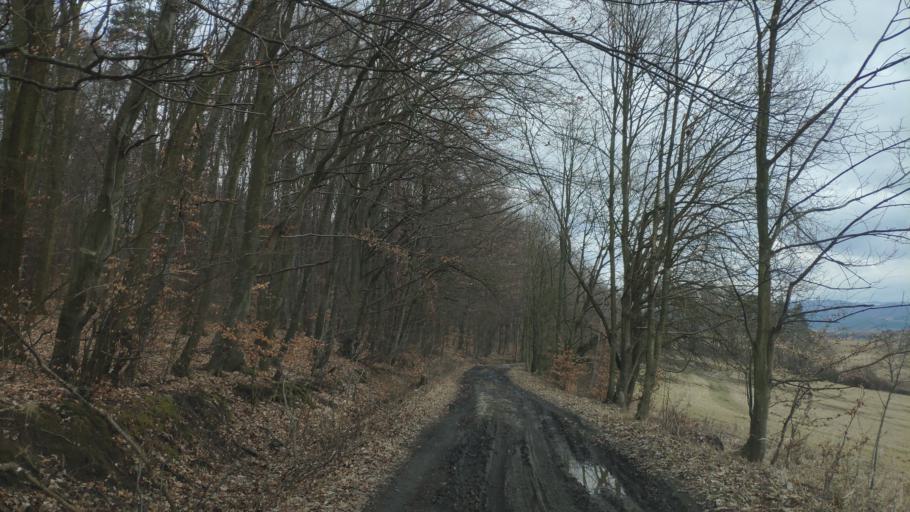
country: SK
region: Presovsky
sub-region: Okres Presov
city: Presov
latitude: 49.0751
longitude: 21.2730
